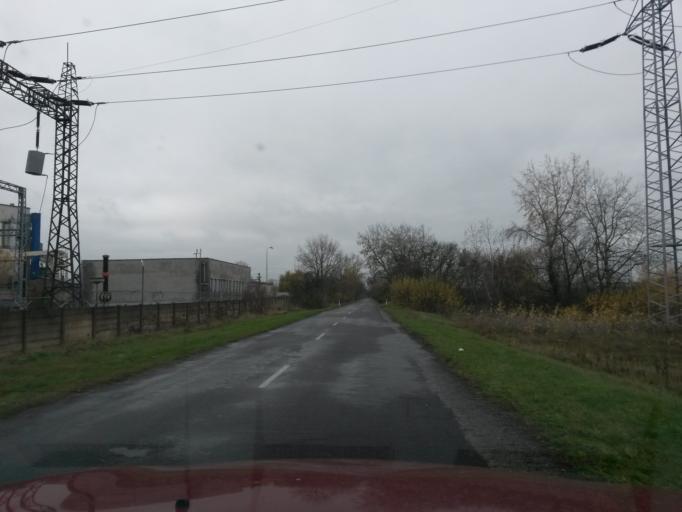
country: SK
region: Kosicky
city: Cierna nad Tisou
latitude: 48.5541
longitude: 21.9706
